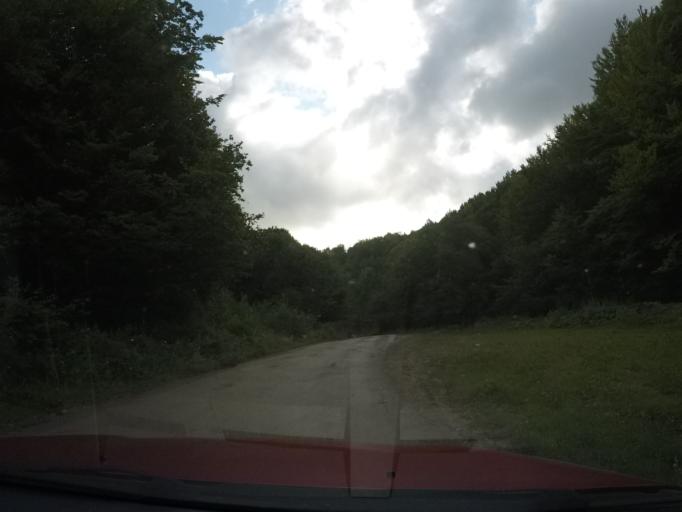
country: UA
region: Zakarpattia
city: Velykyi Bereznyi
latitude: 48.9484
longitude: 22.6548
